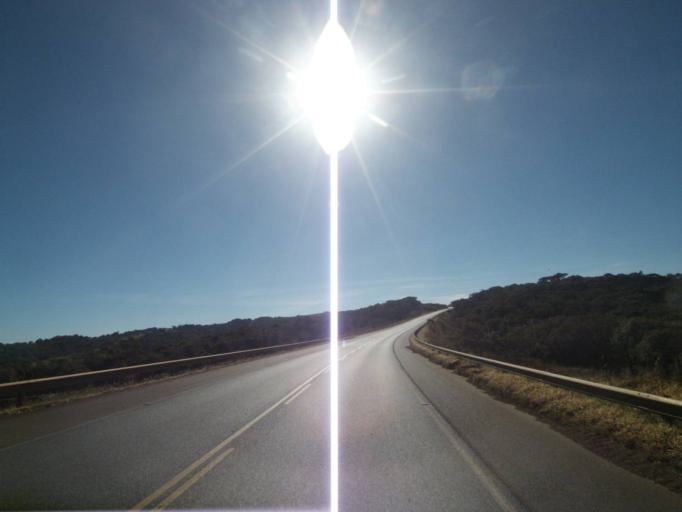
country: BR
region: Parana
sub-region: Tibagi
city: Tibagi
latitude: -24.4024
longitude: -50.3420
